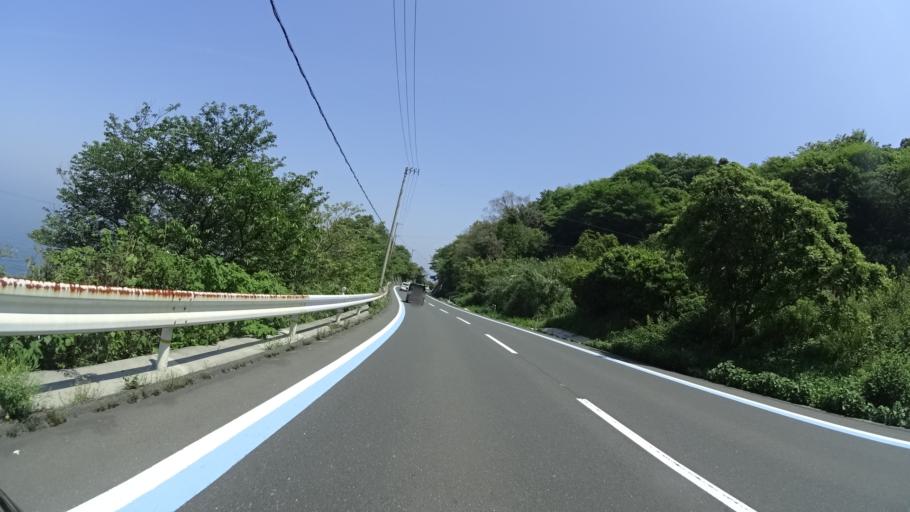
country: JP
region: Ehime
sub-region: Nishiuwa-gun
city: Ikata-cho
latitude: 33.5488
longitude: 132.4247
